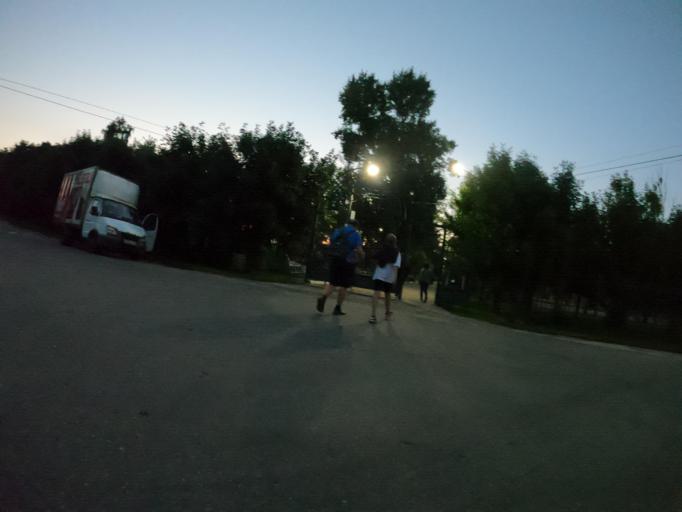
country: RU
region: Moskovskaya
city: Mikhnevo
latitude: 55.1218
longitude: 37.9553
